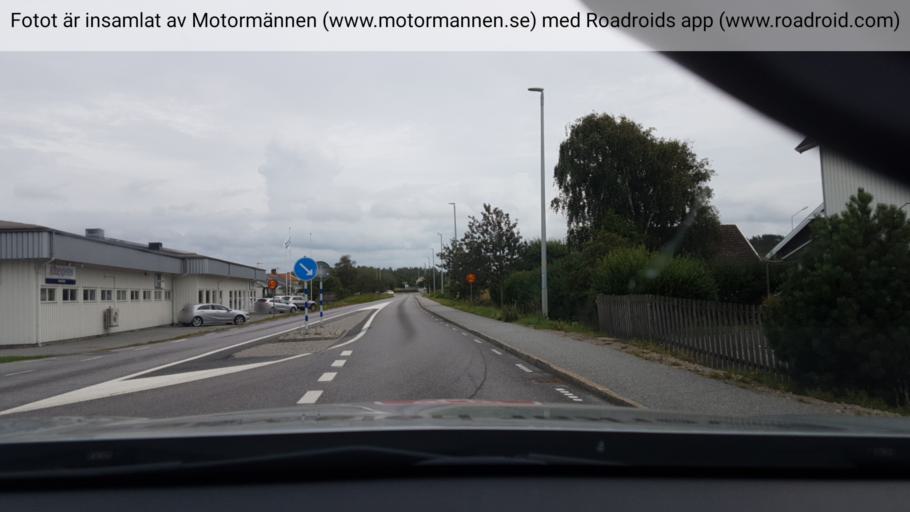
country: SE
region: Vaestra Goetaland
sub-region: Tanums Kommun
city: Grebbestad
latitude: 58.5999
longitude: 11.2891
